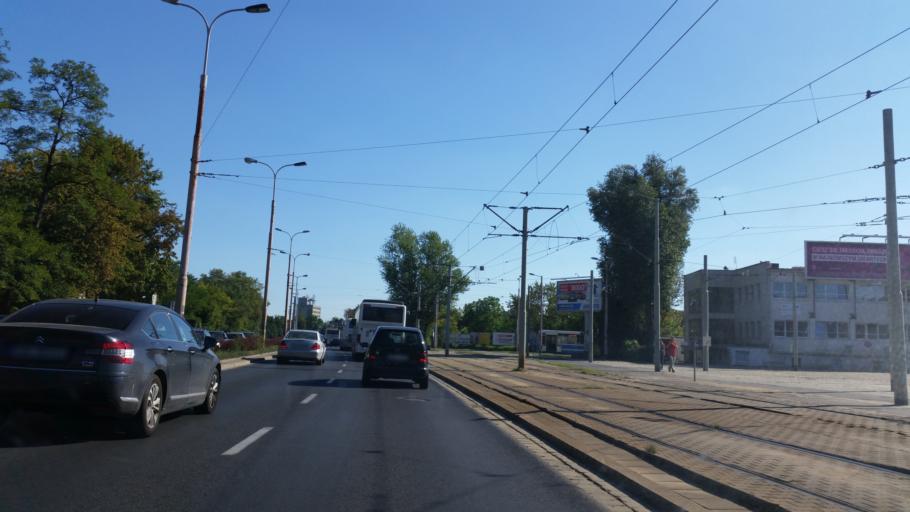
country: PL
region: Lower Silesian Voivodeship
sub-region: Powiat wroclawski
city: Wroclaw
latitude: 51.0790
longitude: 17.0076
